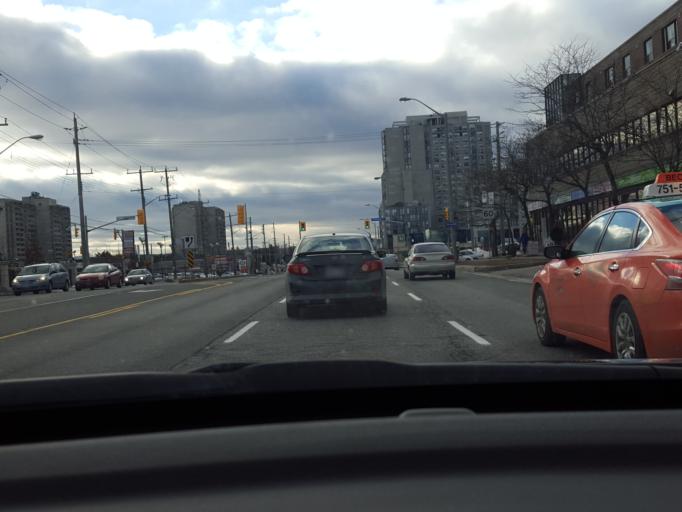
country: CA
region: Ontario
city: Scarborough
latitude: 43.7524
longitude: -79.2616
